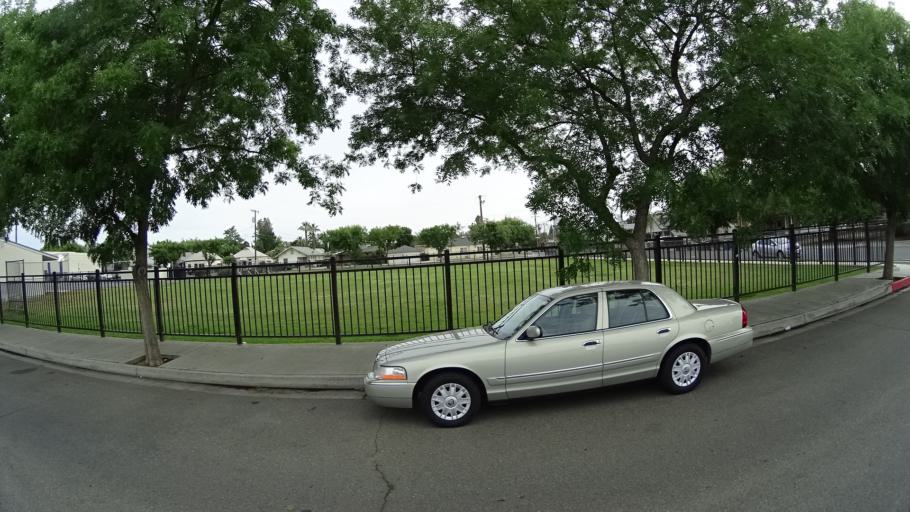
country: US
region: California
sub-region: Kings County
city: Hanford
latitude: 36.3371
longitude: -119.6449
